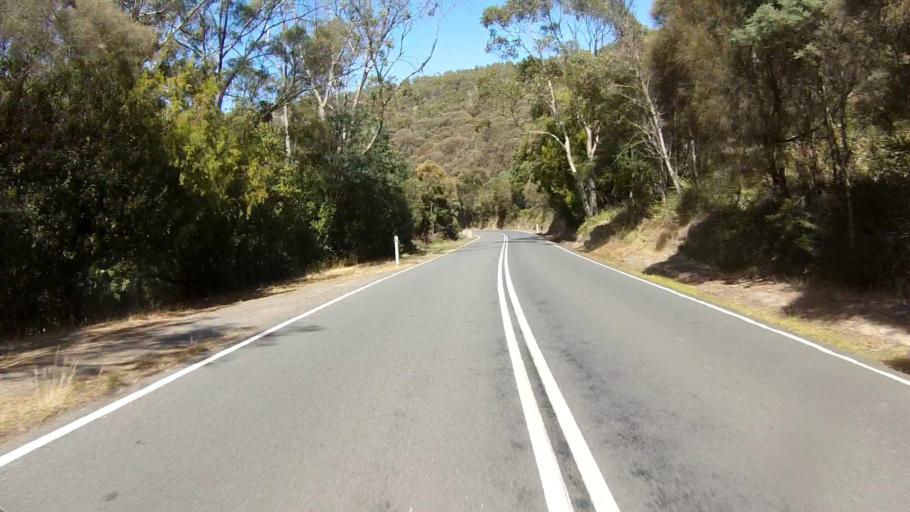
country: AU
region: Tasmania
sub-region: Derwent Valley
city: New Norfolk
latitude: -42.6801
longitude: 146.7664
